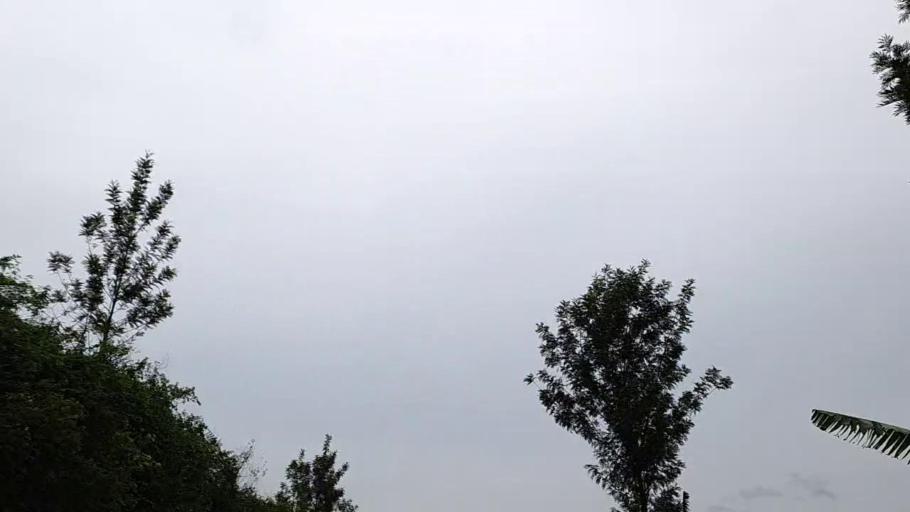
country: RW
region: Kigali
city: Kigali
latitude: -1.9461
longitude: 29.9892
